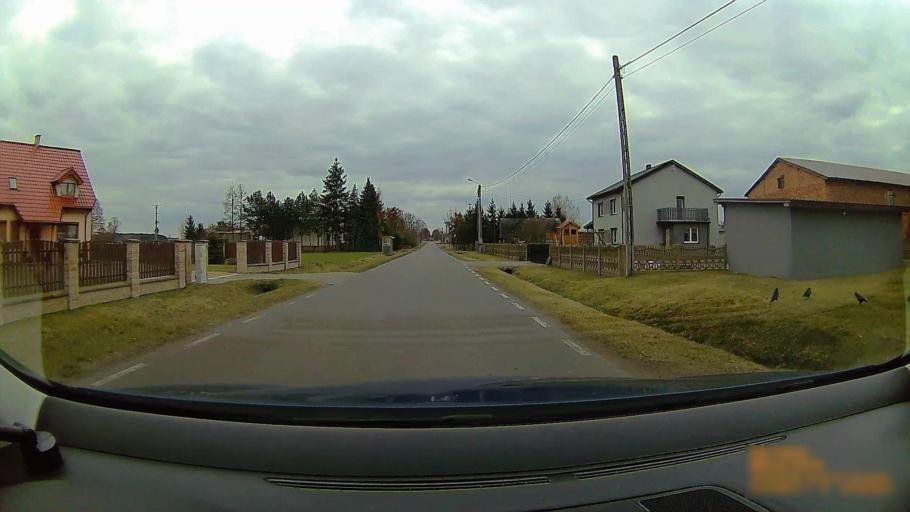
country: PL
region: Greater Poland Voivodeship
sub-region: Powiat koninski
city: Rzgow Pierwszy
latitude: 52.1462
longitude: 18.0554
